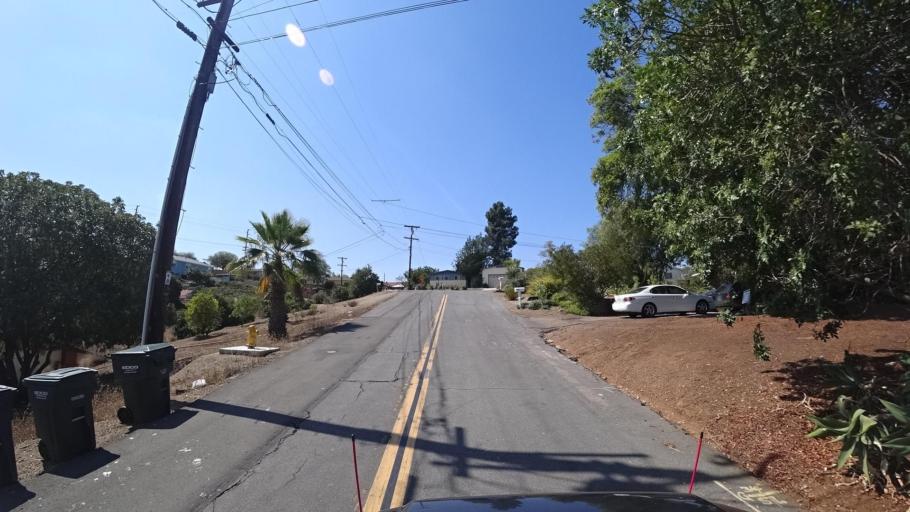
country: US
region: California
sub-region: San Diego County
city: Spring Valley
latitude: 32.7416
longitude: -116.9832
